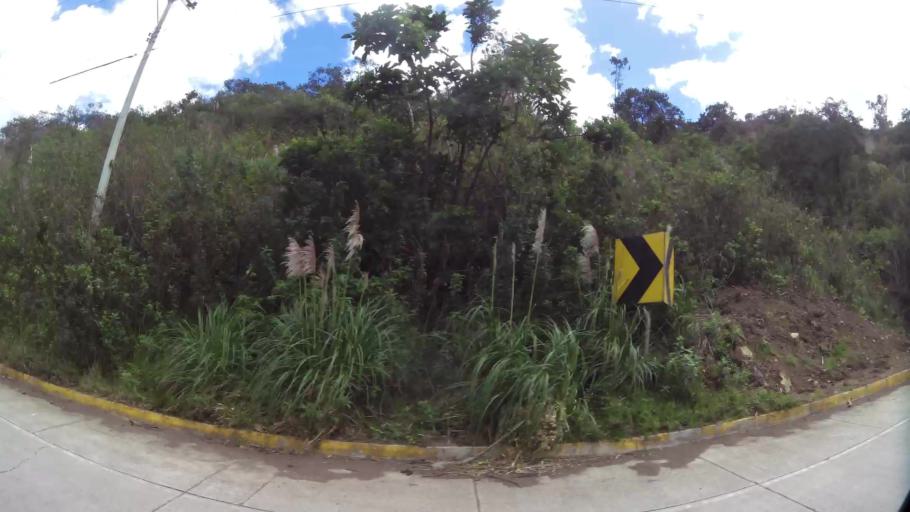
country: EC
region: Azuay
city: Cuenca
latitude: -3.1347
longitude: -79.1204
